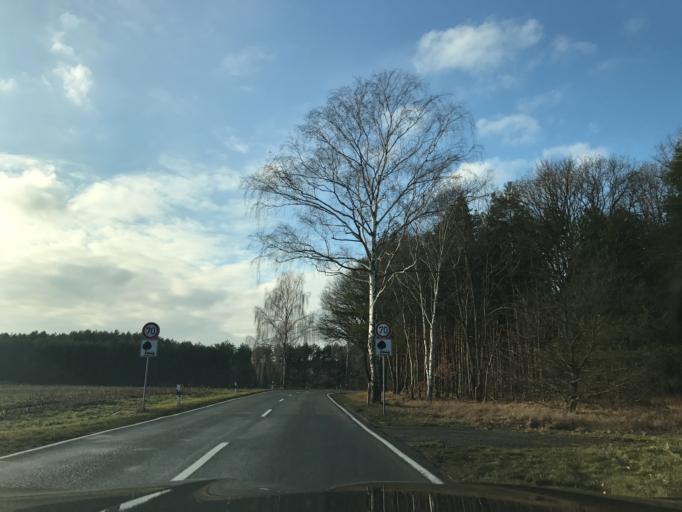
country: DE
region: Brandenburg
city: Ziesar
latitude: 52.2718
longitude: 12.3394
